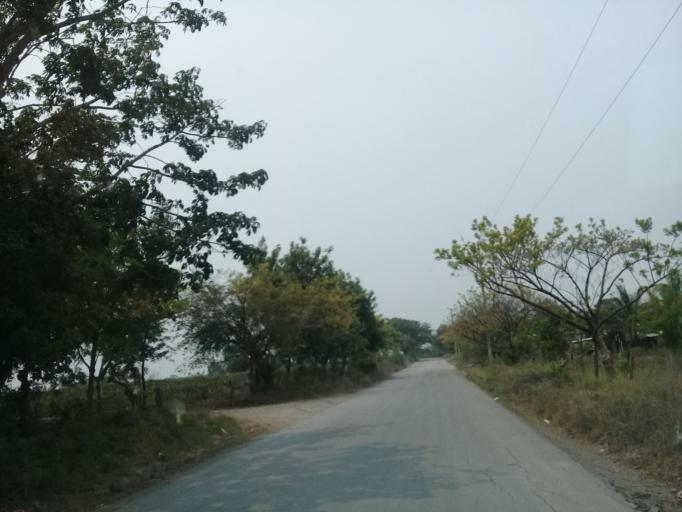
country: MX
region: Veracruz
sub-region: Medellin
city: La Laguna y Monte del Castillo
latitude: 18.9436
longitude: -96.1261
